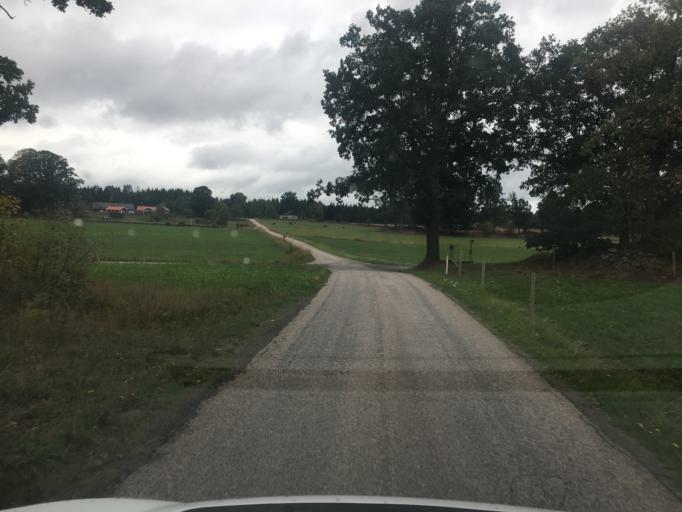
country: SE
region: Kronoberg
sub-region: Ljungby Kommun
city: Lagan
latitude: 56.9776
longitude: 14.0371
